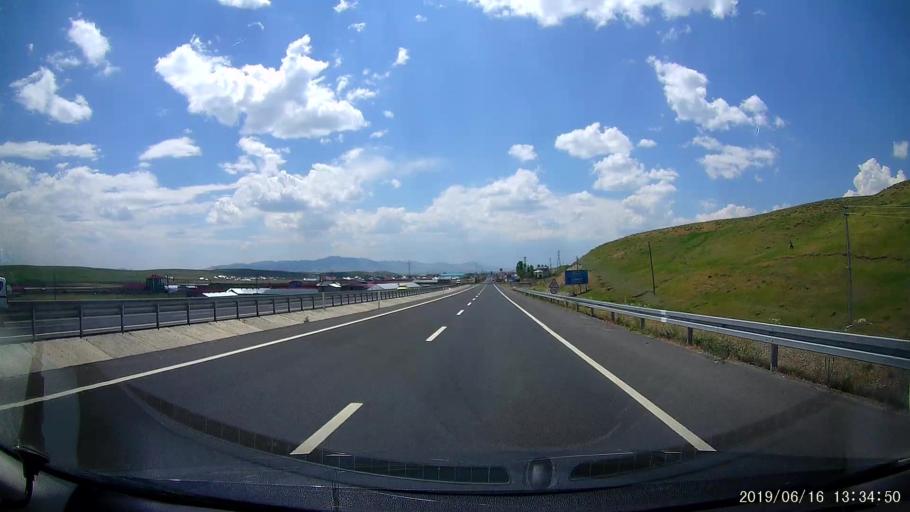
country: TR
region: Agri
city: Agri
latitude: 39.7129
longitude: 43.1165
